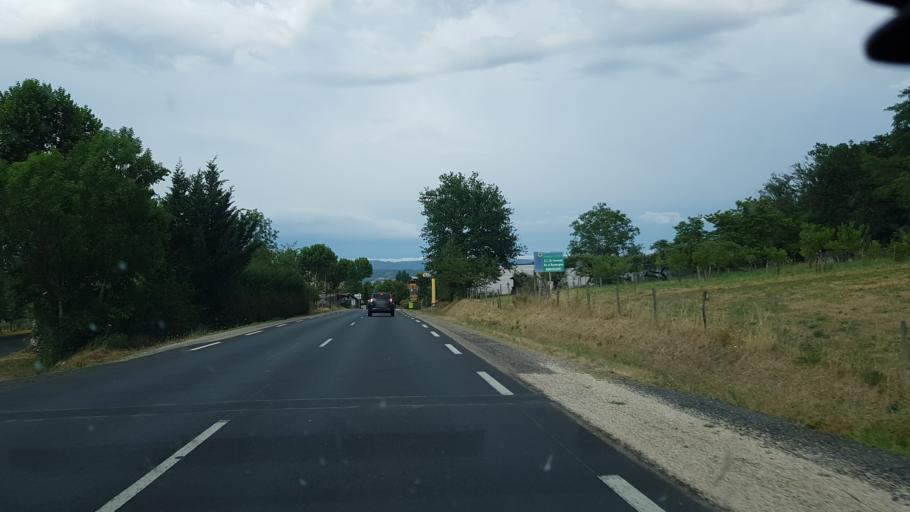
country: FR
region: Auvergne
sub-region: Departement de la Haute-Loire
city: Brioude
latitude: 45.2886
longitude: 3.3660
